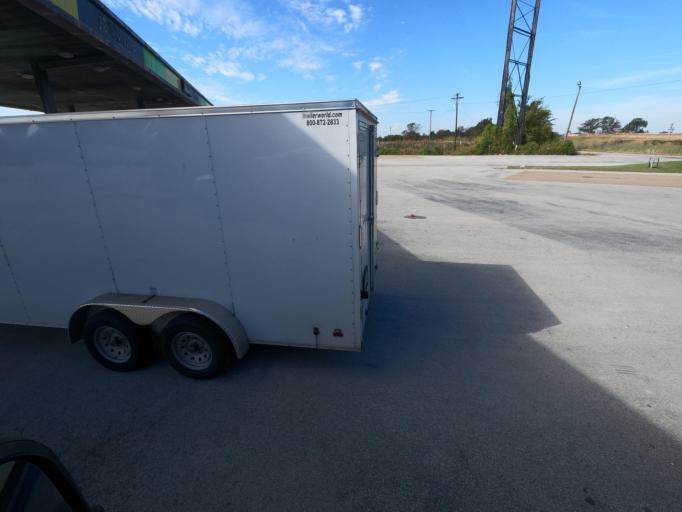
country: US
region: Tennessee
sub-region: Crockett County
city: Bells
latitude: 35.5839
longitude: -89.0912
